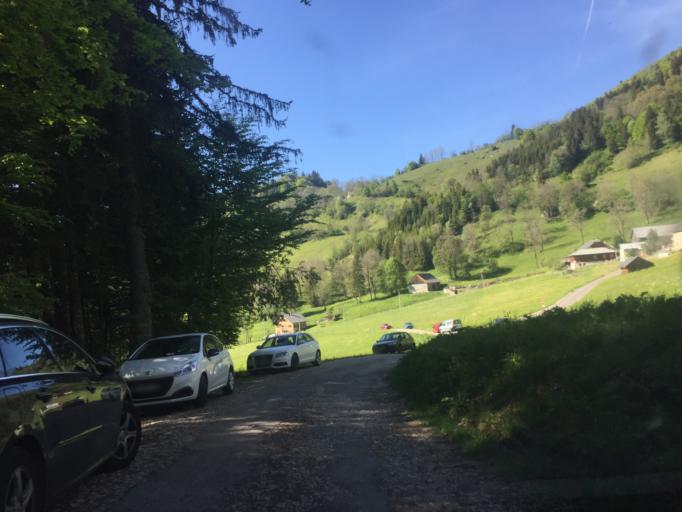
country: FR
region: Rhone-Alpes
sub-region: Departement de l'Isere
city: Barraux
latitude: 45.4417
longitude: 5.9057
